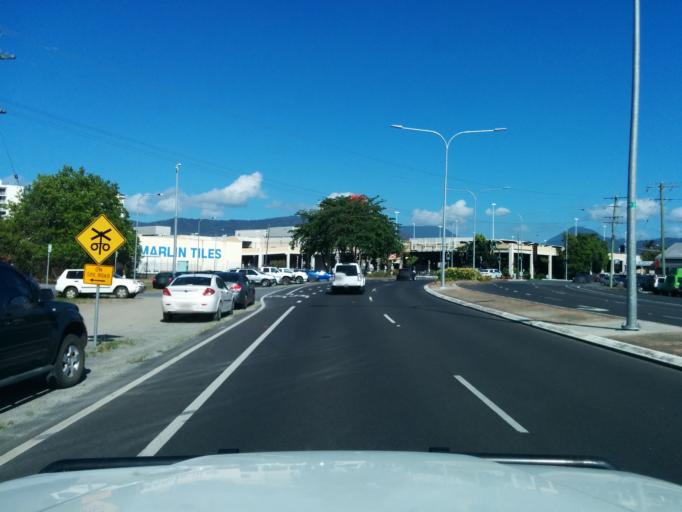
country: AU
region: Queensland
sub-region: Cairns
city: Cairns
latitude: -16.9238
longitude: 145.7686
